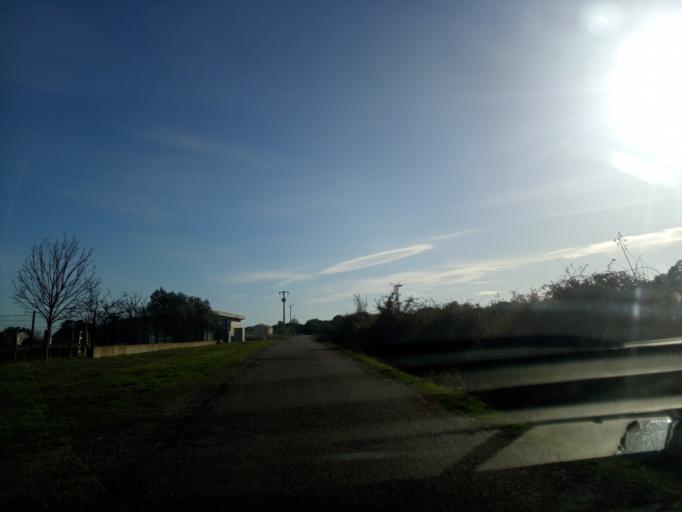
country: FR
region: Corsica
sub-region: Departement de la Haute-Corse
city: Linguizzetta
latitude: 42.2633
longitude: 9.5443
